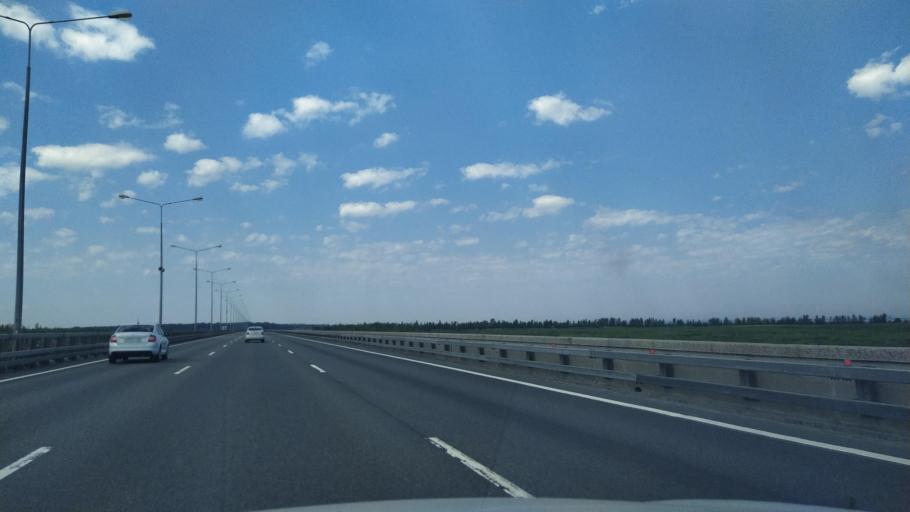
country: RU
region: St.-Petersburg
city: Kronshtadt
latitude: 60.0208
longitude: 29.7577
